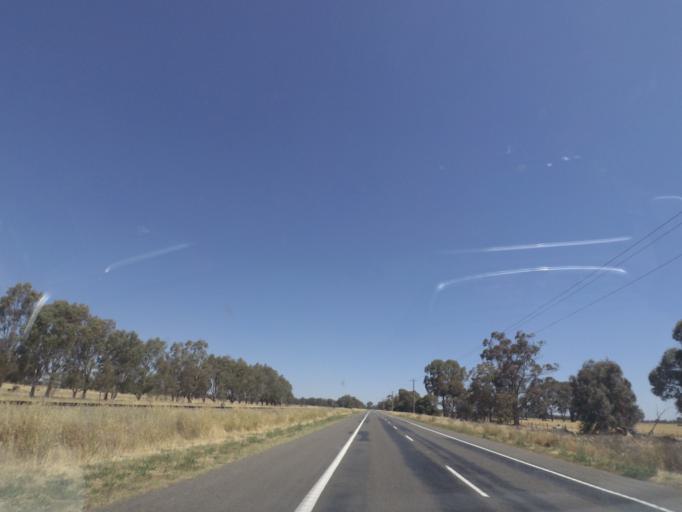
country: AU
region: Victoria
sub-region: Greater Shepparton
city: Shepparton
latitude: -36.2181
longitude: 145.4318
